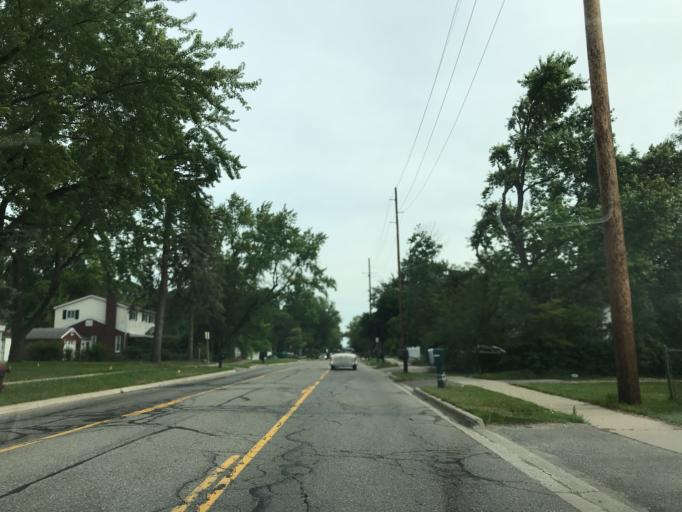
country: US
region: Michigan
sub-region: Oakland County
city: Farmington
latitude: 42.4486
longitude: -83.3172
